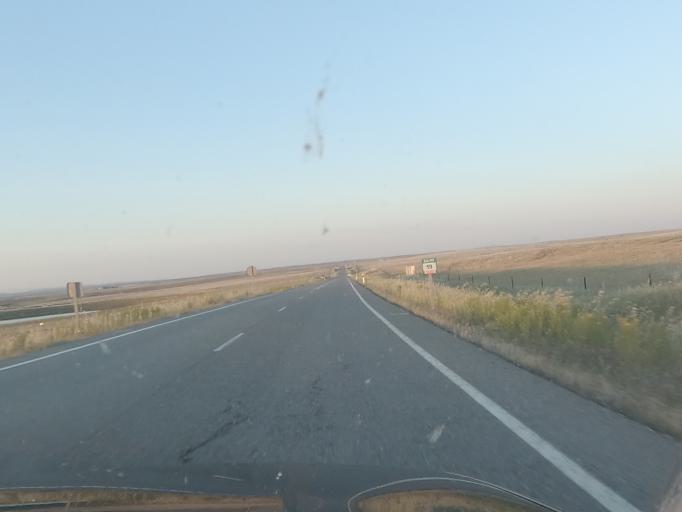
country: ES
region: Extremadura
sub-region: Provincia de Caceres
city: Alcantara
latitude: 39.6264
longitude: -6.9313
